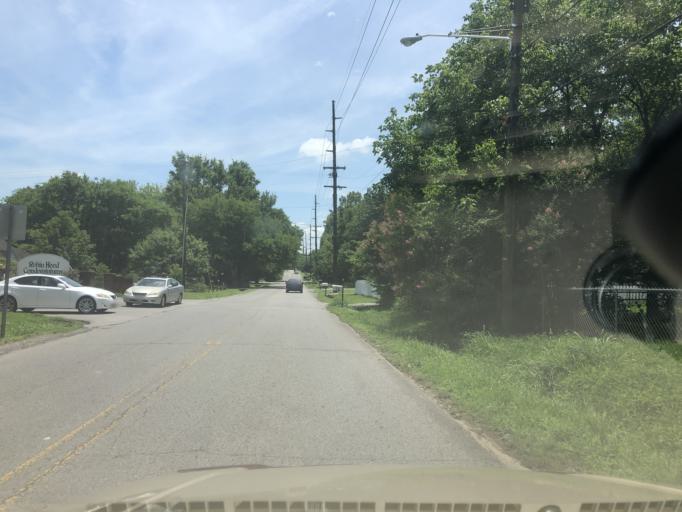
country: US
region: Tennessee
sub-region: Davidson County
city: Goodlettsville
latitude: 36.2594
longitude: -86.7038
